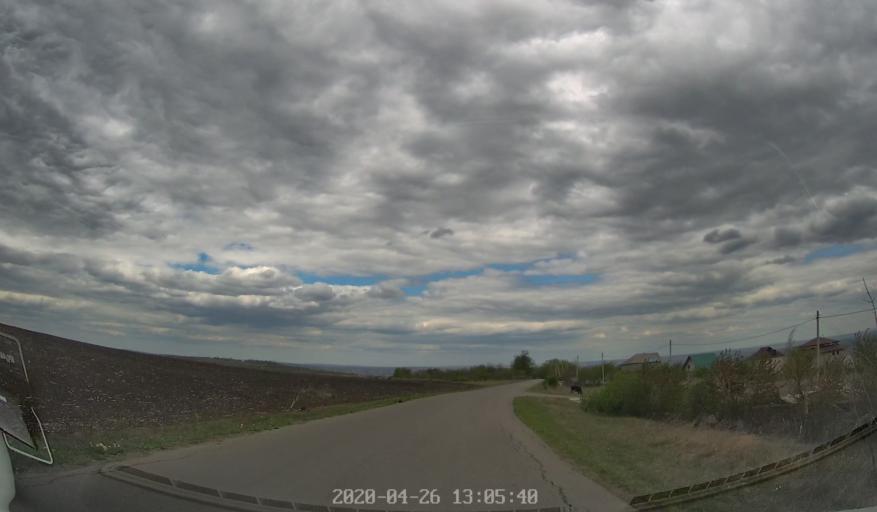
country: MD
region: Chisinau
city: Vadul lui Voda
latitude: 47.0778
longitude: 29.0667
